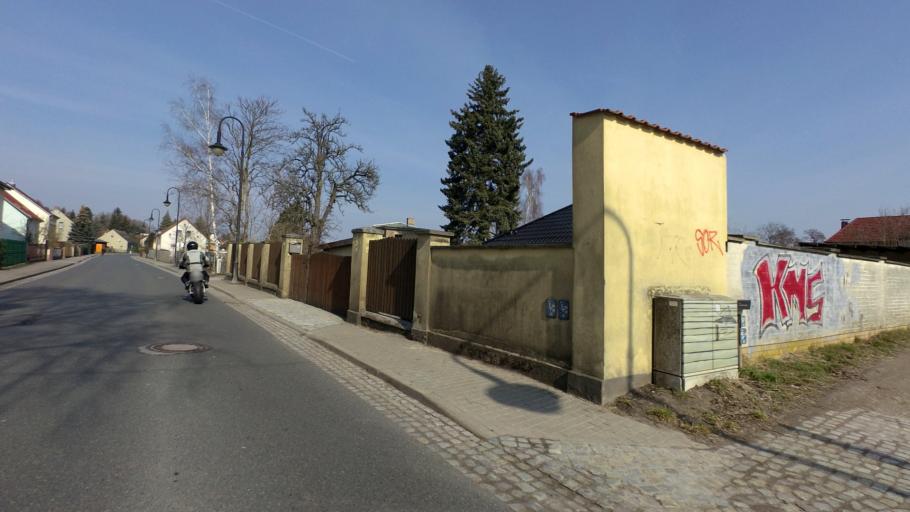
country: DE
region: Brandenburg
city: Werder
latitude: 52.3671
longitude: 12.9392
